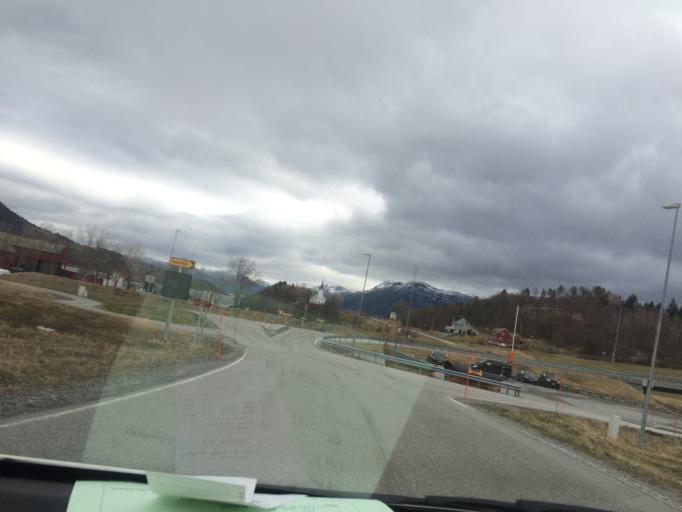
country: NO
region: More og Romsdal
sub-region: Gjemnes
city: Batnfjordsora
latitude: 62.9637
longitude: 7.7667
